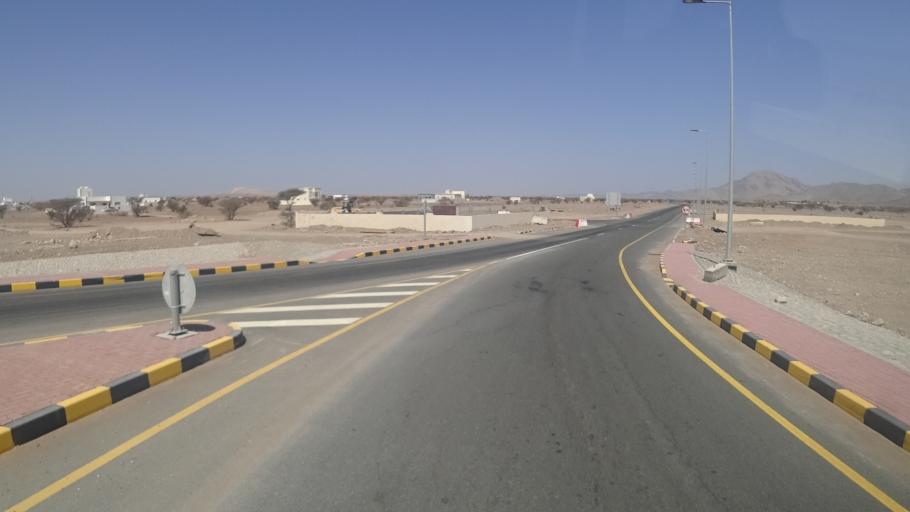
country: OM
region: Ash Sharqiyah
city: Badiyah
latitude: 22.4976
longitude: 58.9466
